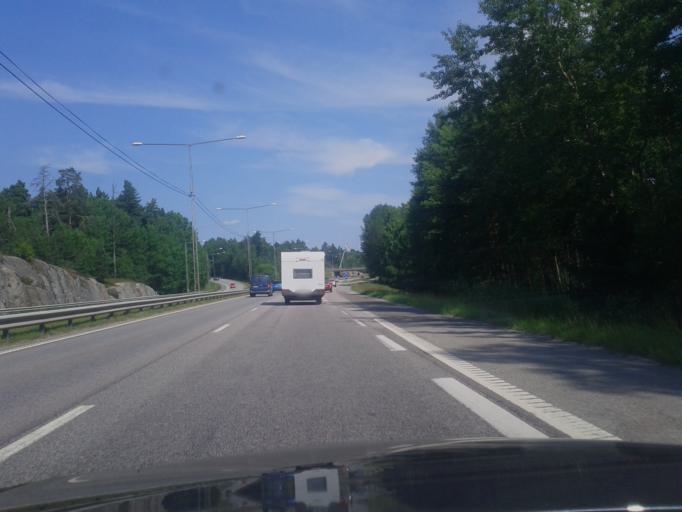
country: SE
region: Stockholm
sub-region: Taby Kommun
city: Taby
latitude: 59.4519
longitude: 18.1326
